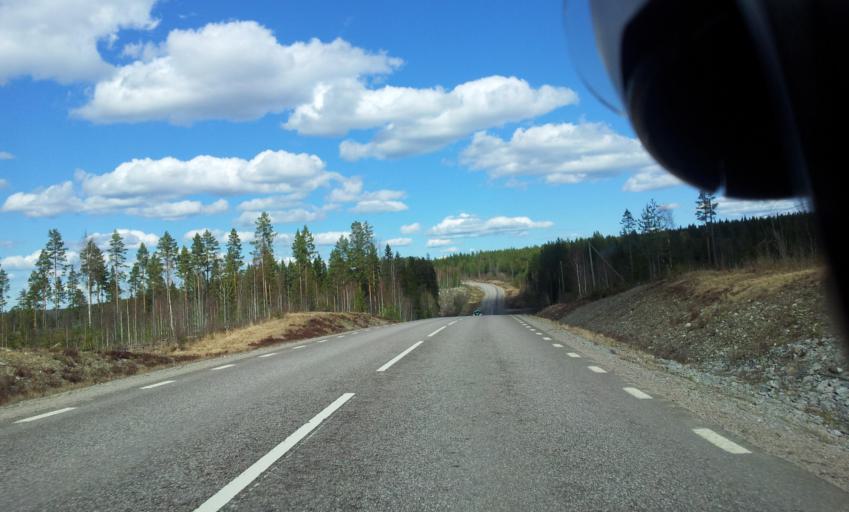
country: SE
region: Gaevleborg
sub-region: Ovanakers Kommun
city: Edsbyn
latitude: 61.2116
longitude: 15.8713
